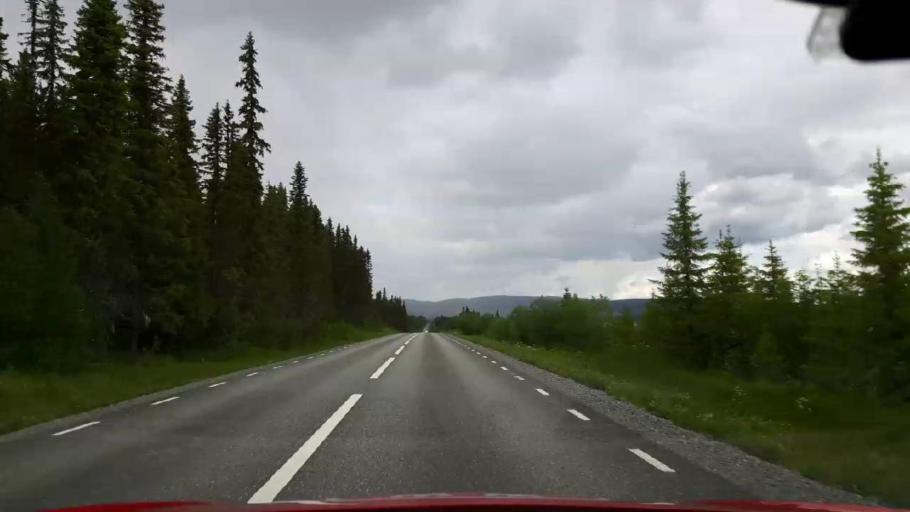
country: SE
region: Jaemtland
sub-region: Krokoms Kommun
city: Krokom
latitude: 63.7039
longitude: 14.3146
